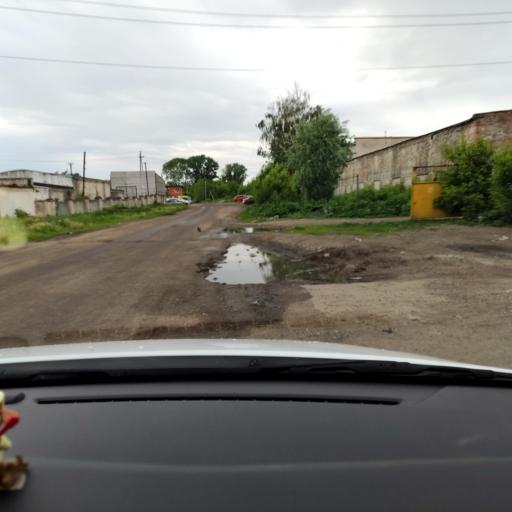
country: RU
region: Tatarstan
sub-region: Gorod Kazan'
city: Kazan
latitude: 55.7305
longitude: 49.1034
